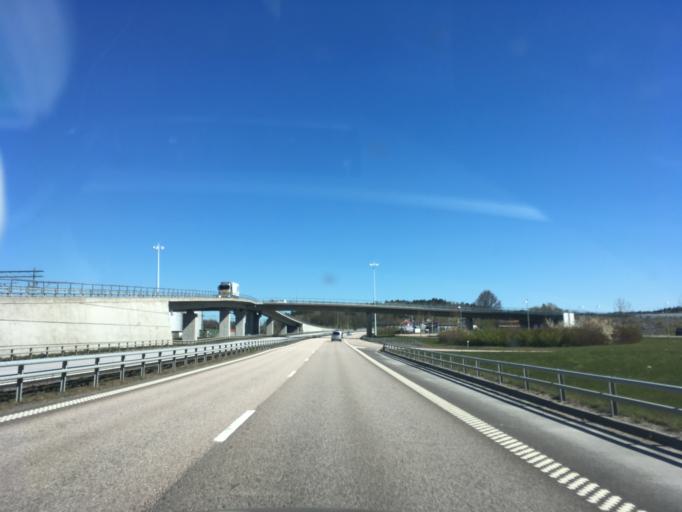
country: SE
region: Vaestra Goetaland
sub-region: Ale Kommun
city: Nodinge-Nol
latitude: 57.9195
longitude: 12.0630
